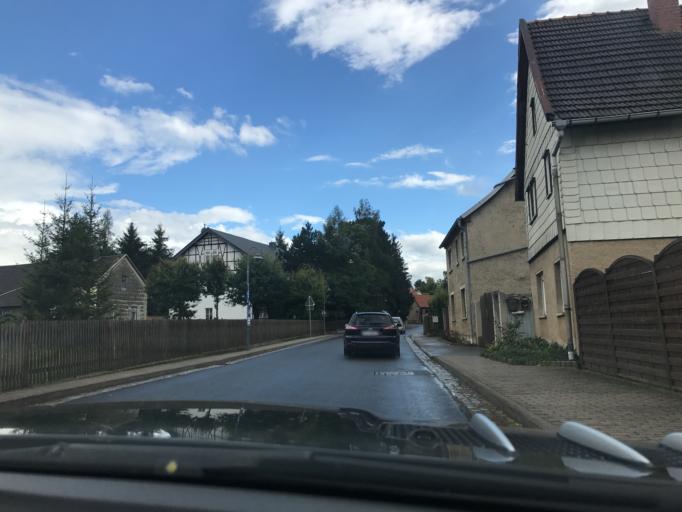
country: DE
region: Thuringia
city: Mulverstedt
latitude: 51.1095
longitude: 10.5118
